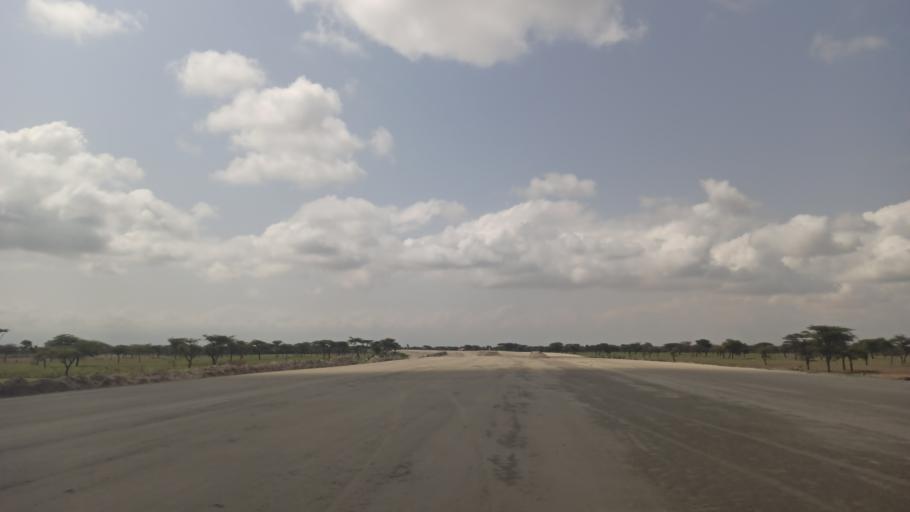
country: ET
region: Oromiya
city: Ziway
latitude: 7.6970
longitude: 38.6450
